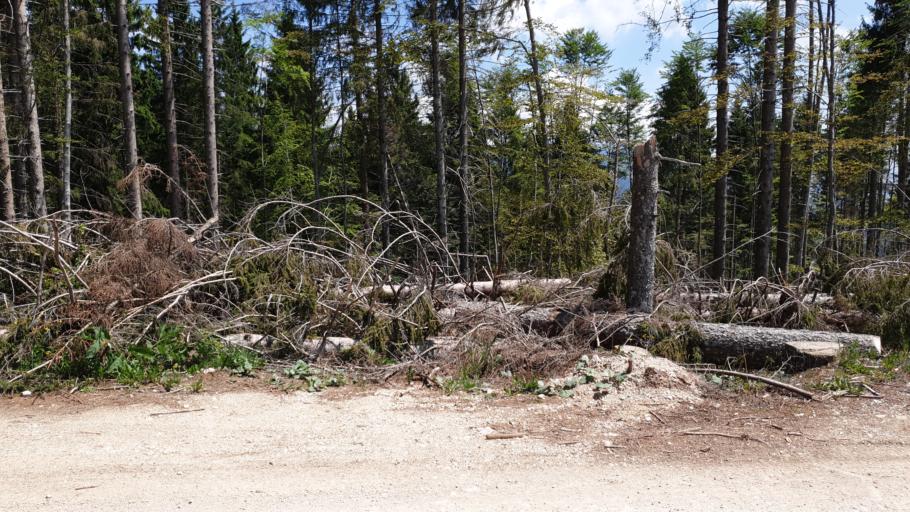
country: IT
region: Veneto
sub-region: Provincia di Vicenza
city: Canove di Roana
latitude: 45.8973
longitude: 11.4817
